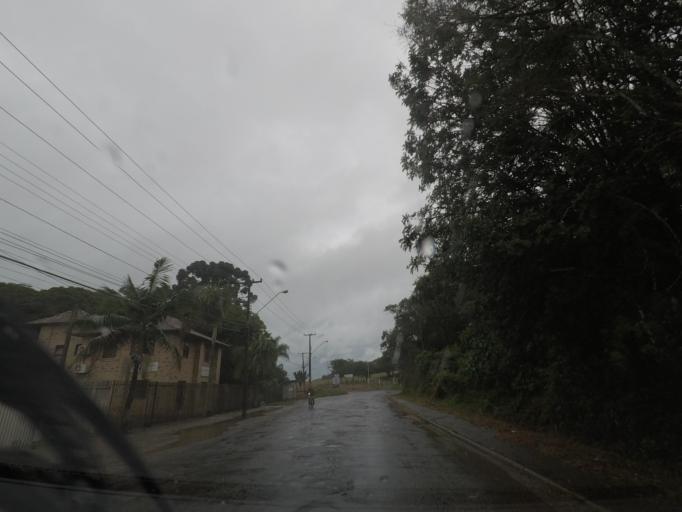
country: BR
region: Parana
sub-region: Campo Largo
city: Campo Largo
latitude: -25.4602
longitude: -49.4226
